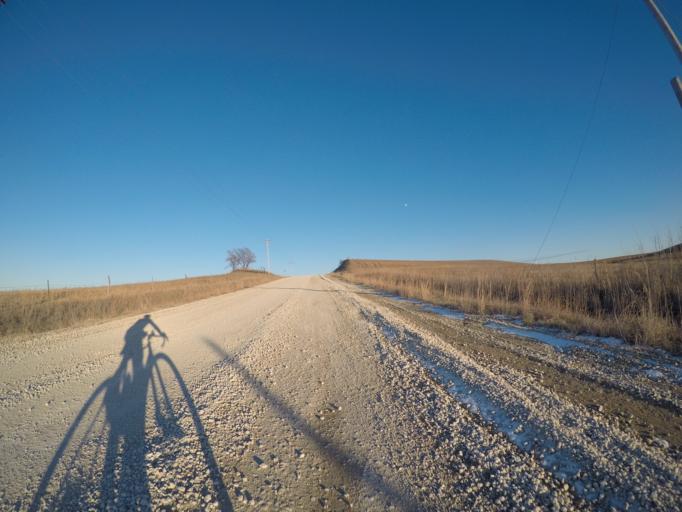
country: US
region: Kansas
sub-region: Pottawatomie County
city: Westmoreland
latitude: 39.3199
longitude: -96.5197
